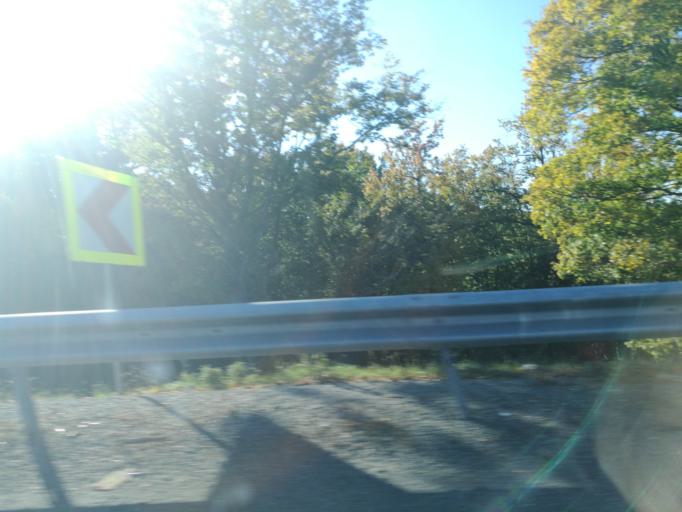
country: RO
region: Brasov
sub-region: Comuna Dumbravita
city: Dumbravita
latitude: 45.7523
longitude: 25.3949
